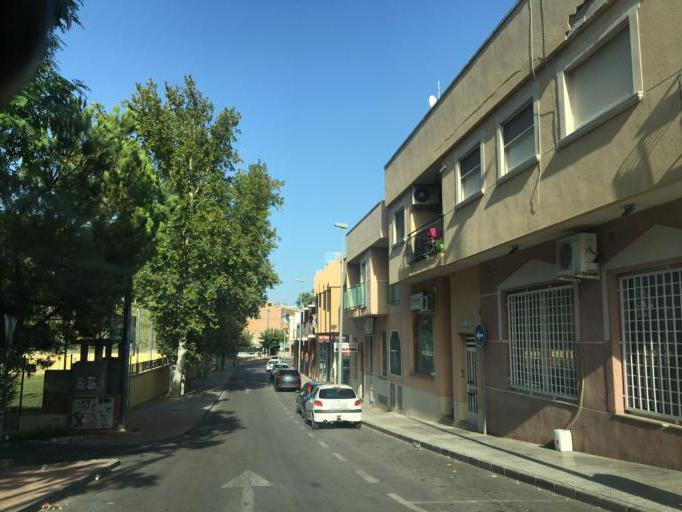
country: ES
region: Murcia
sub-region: Murcia
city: Santomera
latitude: 38.0365
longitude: -1.0773
